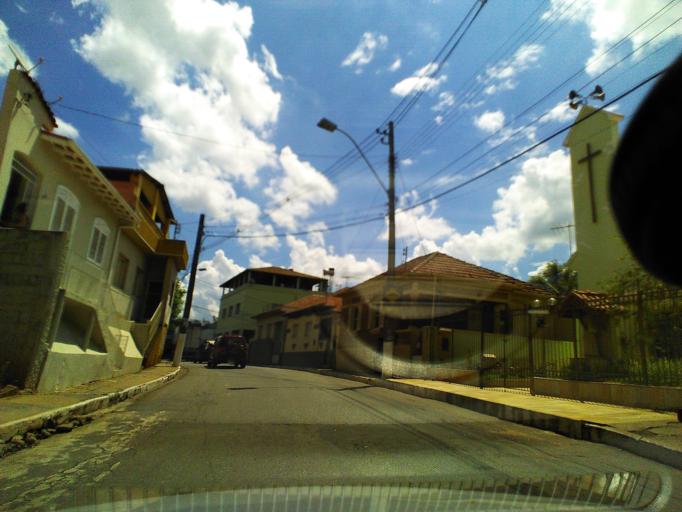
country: BR
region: Minas Gerais
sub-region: Tres Coracoes
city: Tres Coracoes
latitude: -21.7000
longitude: -45.2621
